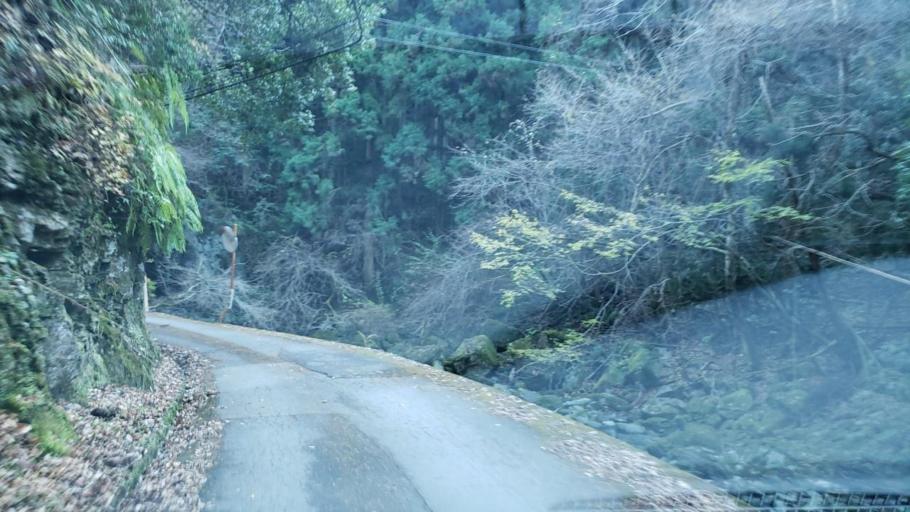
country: JP
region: Tokushima
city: Wakimachi
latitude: 33.9878
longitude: 133.9850
